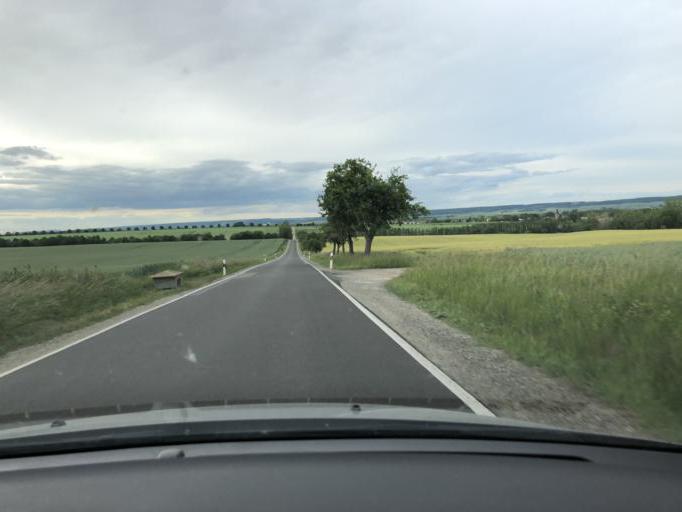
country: DE
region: Thuringia
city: Willerstedt
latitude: 51.0766
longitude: 11.4465
